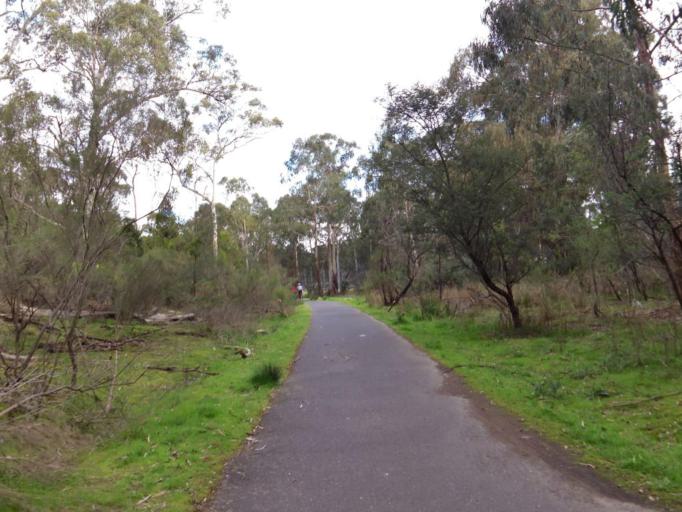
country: AU
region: Victoria
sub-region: Nillumbik
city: Eltham
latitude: -37.7496
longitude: 145.1740
